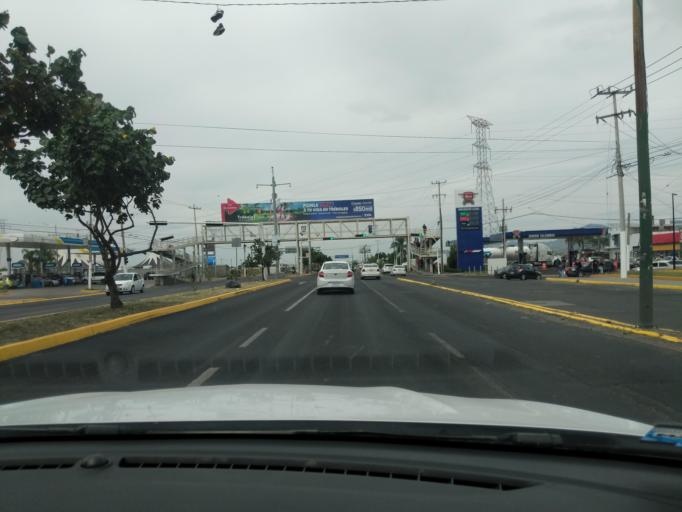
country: MX
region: Jalisco
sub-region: Zapopan
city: La Cuchilla (Extramuros de Tesistan)
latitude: 20.7765
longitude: -103.4560
